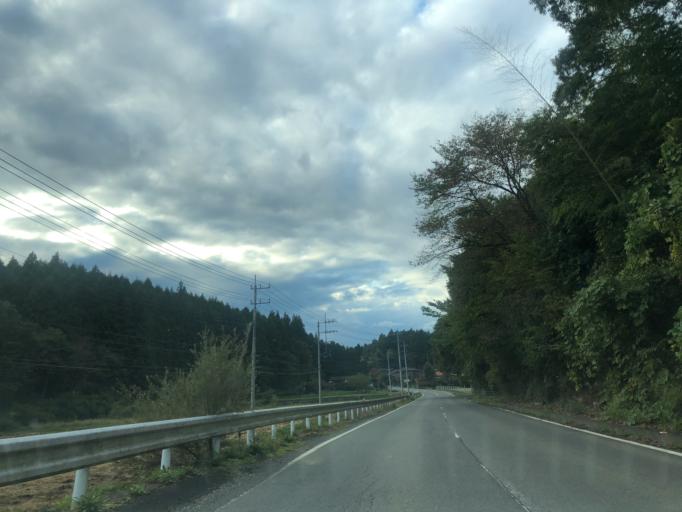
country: JP
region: Tochigi
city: Kuroiso
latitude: 36.9395
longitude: 140.1207
